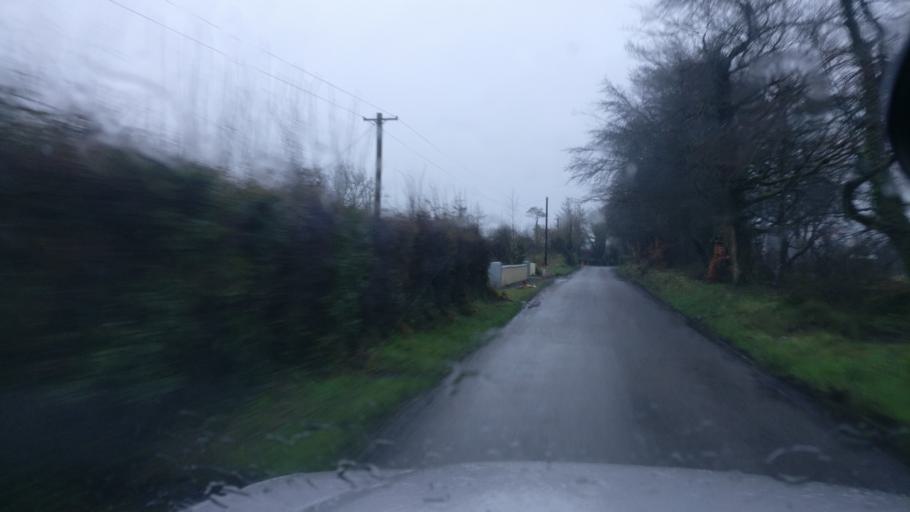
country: IE
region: Connaught
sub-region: County Galway
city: Ballinasloe
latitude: 53.3124
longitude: -8.3644
